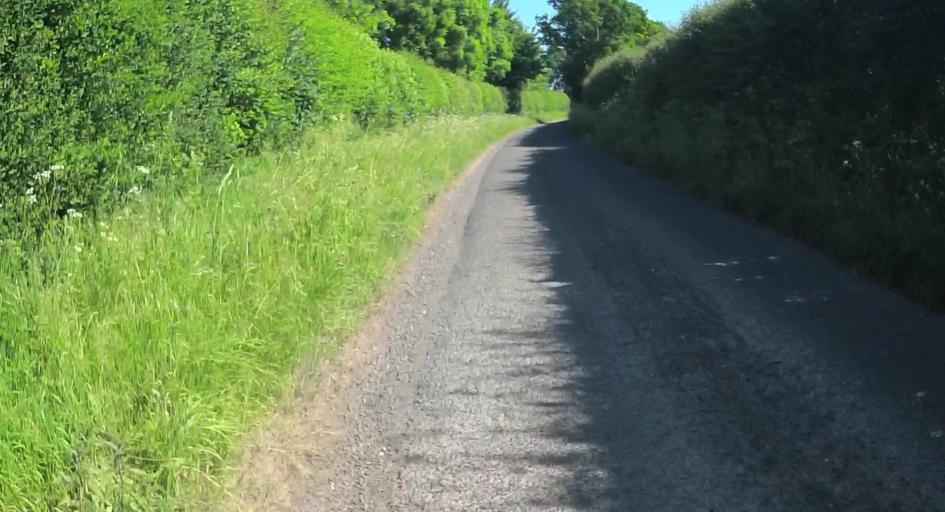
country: GB
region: England
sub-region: Hampshire
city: Overton
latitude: 51.2759
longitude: -1.2533
